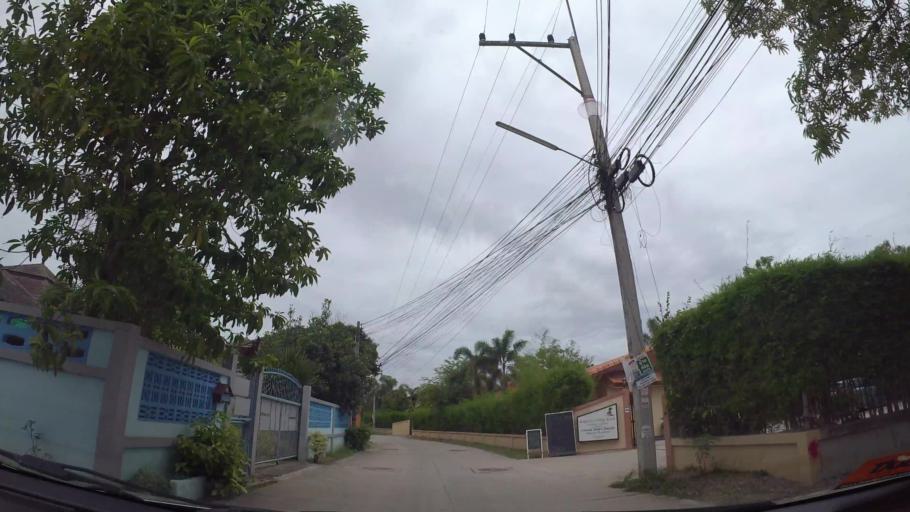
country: TH
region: Chon Buri
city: Sattahip
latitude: 12.7591
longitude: 100.8905
